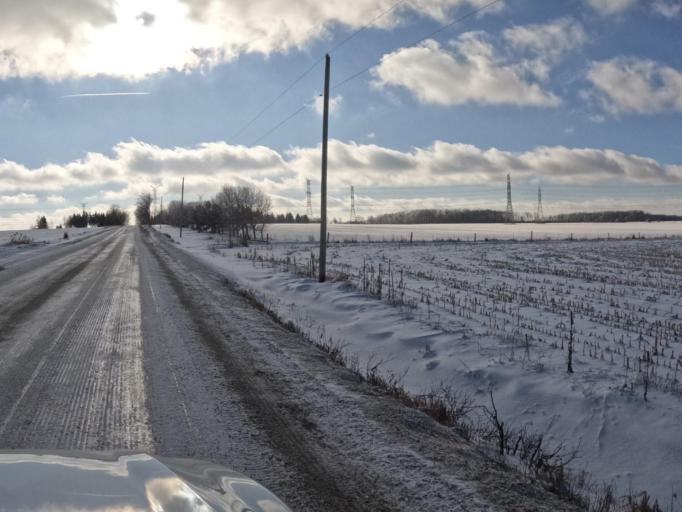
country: CA
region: Ontario
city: Shelburne
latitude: 44.0007
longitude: -80.4096
